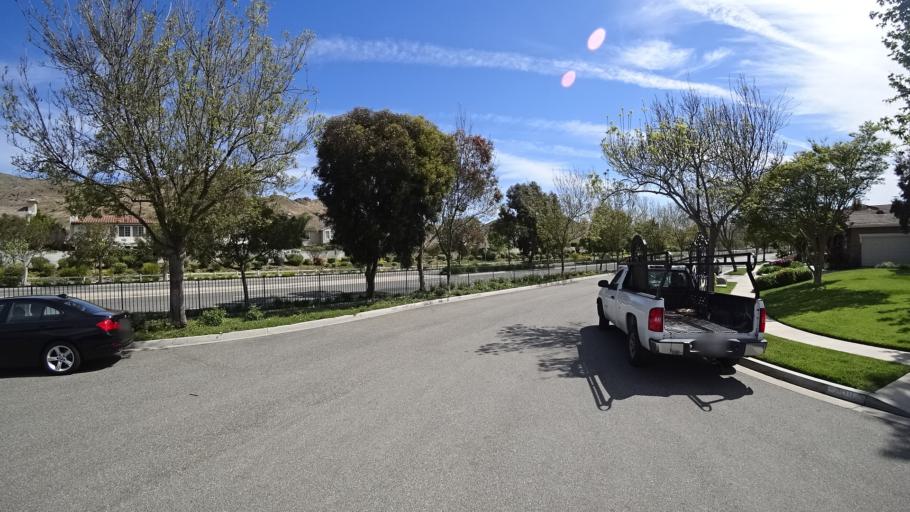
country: US
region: California
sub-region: Ventura County
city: Casa Conejo
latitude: 34.1735
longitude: -118.9810
